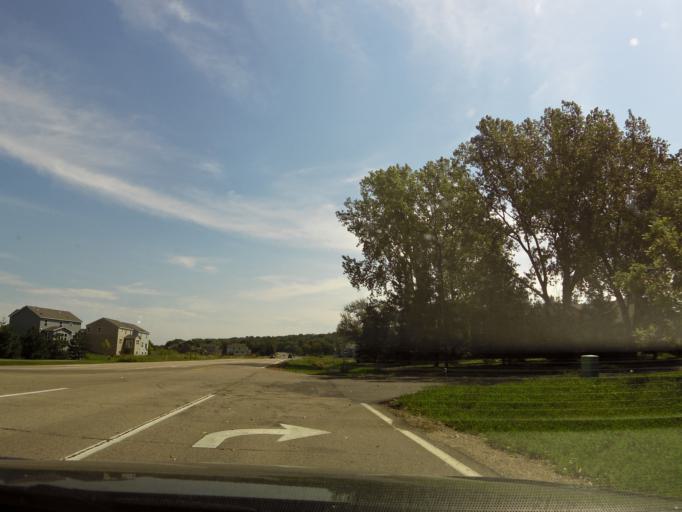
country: US
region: Minnesota
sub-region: Scott County
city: Prior Lake
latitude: 44.7653
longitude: -93.4202
